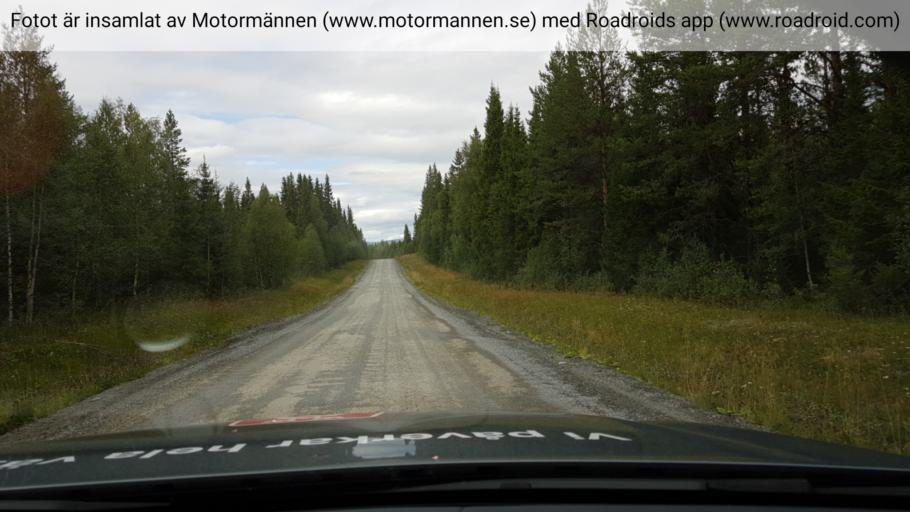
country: SE
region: Jaemtland
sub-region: Krokoms Kommun
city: Valla
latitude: 63.6585
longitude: 13.7614
